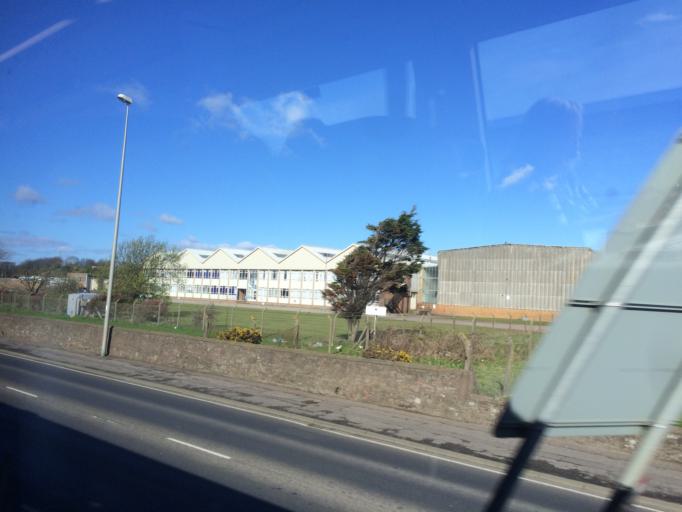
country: GB
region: Scotland
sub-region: Angus
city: Arbroath
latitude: 56.5484
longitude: -2.6137
